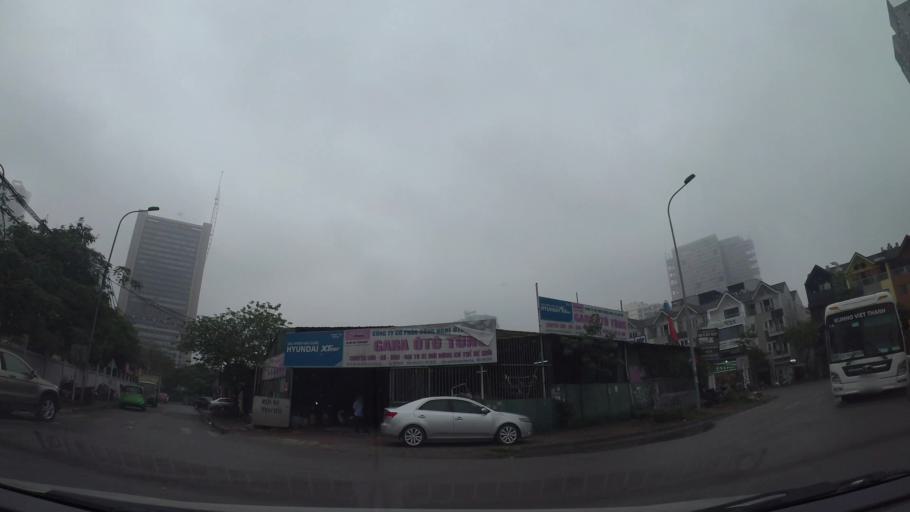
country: VN
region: Ha Noi
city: Cau Giay
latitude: 21.0181
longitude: 105.7868
